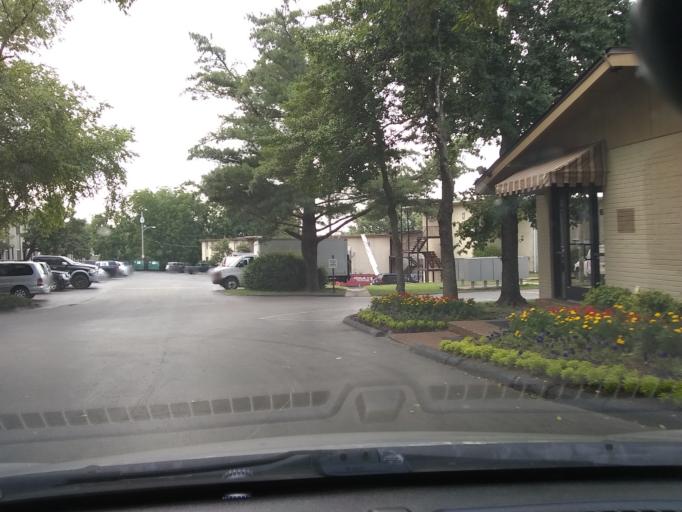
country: US
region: Tennessee
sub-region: Davidson County
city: Oak Hill
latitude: 36.1182
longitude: -86.7029
